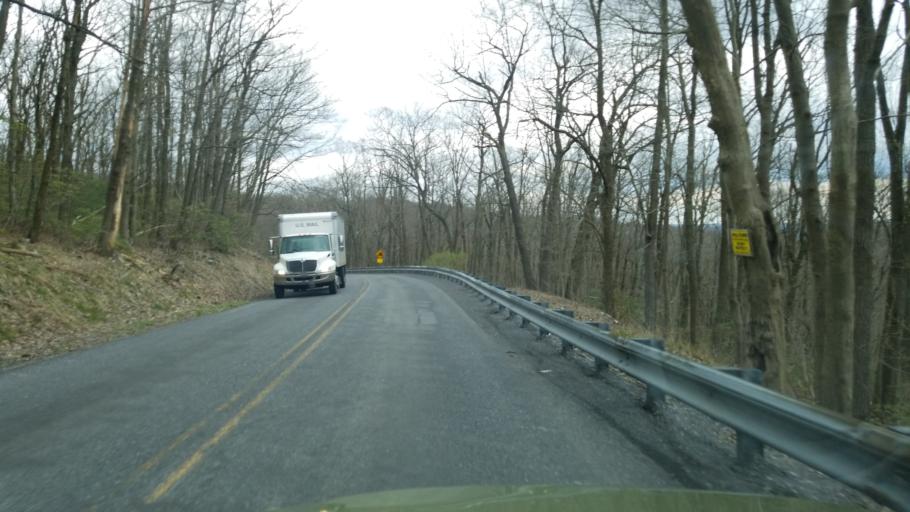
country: US
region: Pennsylvania
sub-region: Blair County
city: Tipton
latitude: 40.7206
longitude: -78.3509
